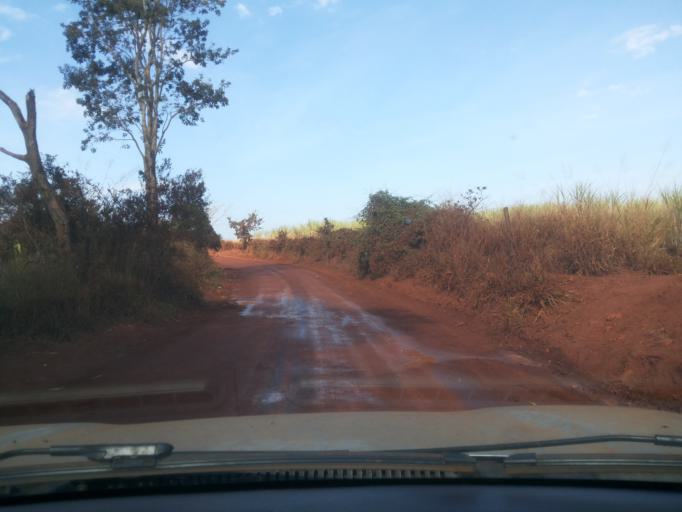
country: BR
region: Minas Gerais
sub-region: Ituiutaba
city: Ituiutaba
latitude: -19.0165
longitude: -49.3969
